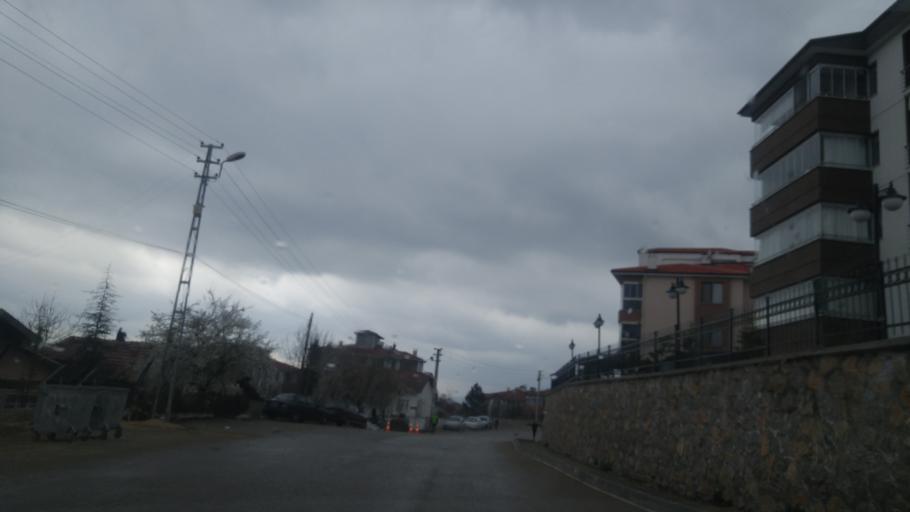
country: TR
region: Karabuk
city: Safranbolu
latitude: 41.2725
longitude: 32.6776
